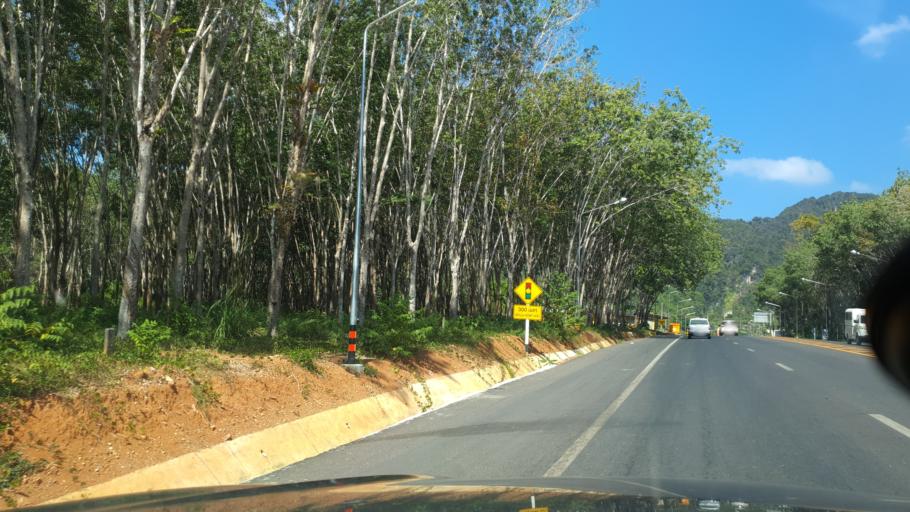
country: TH
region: Krabi
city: Krabi
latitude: 8.0762
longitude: 98.8579
